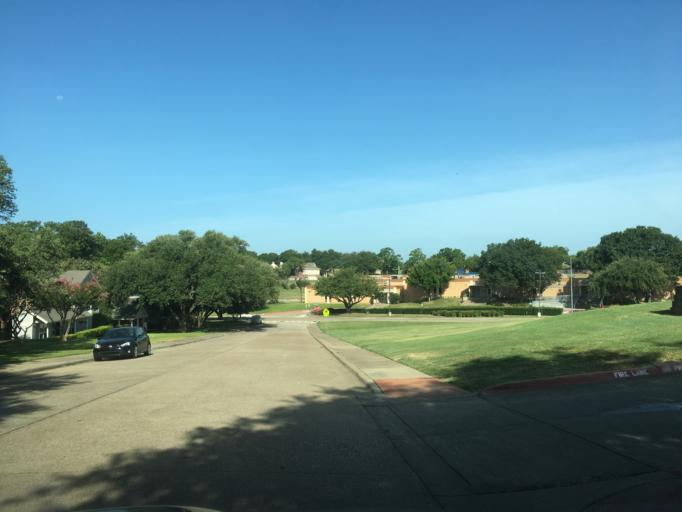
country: US
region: Texas
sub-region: Dallas County
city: Richardson
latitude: 32.8847
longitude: -96.7183
